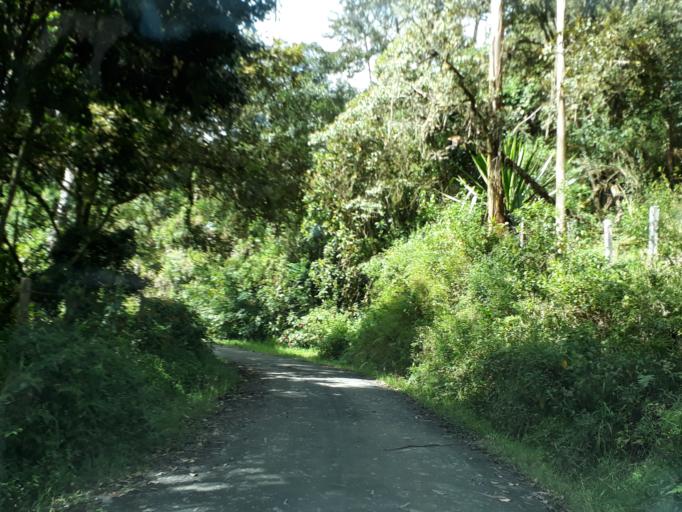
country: CO
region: Cundinamarca
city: Junin
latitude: 4.7610
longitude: -73.6276
